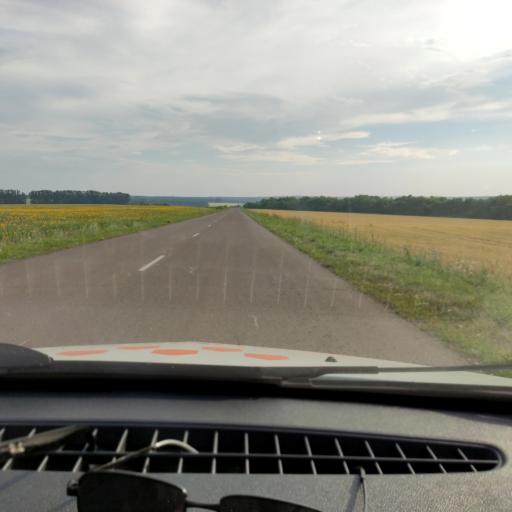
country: RU
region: Bashkortostan
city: Avdon
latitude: 54.5465
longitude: 55.6536
